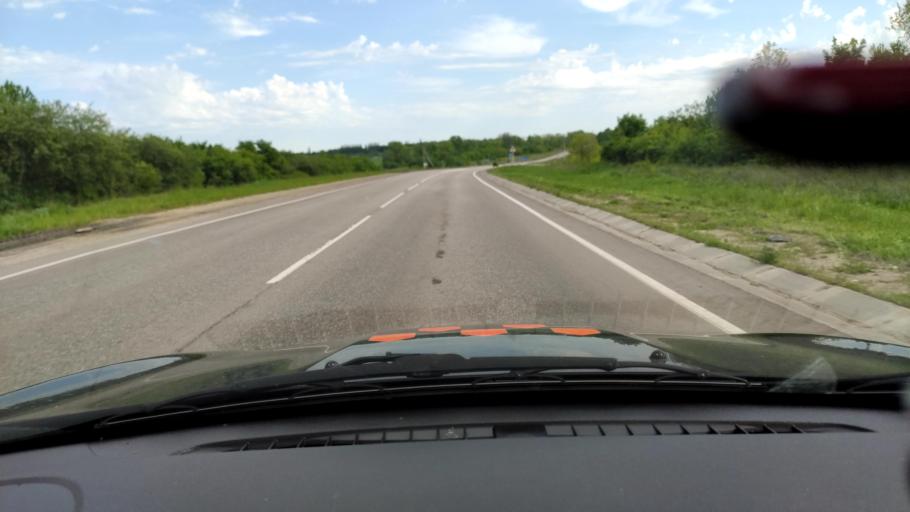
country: RU
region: Voronezj
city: Kolodeznyy
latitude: 51.3720
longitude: 39.0226
